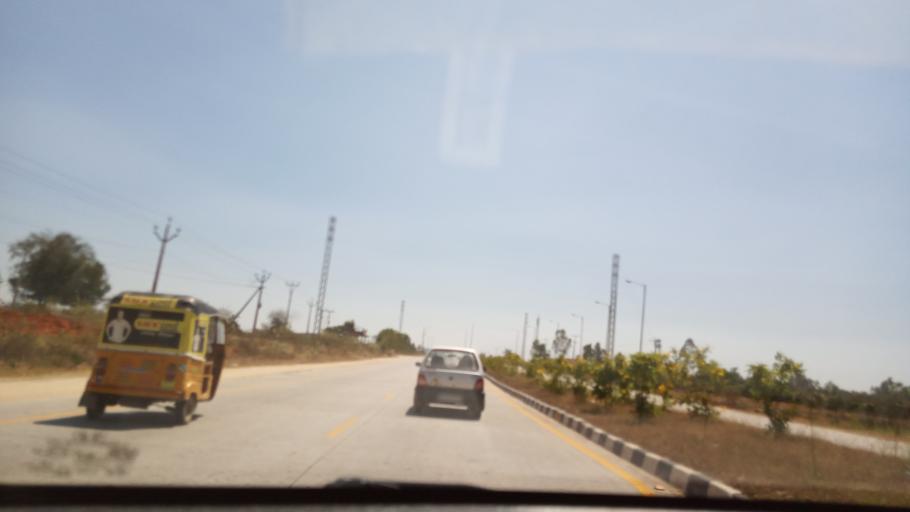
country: IN
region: Andhra Pradesh
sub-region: Chittoor
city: Palmaner
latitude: 13.1903
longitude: 78.5919
